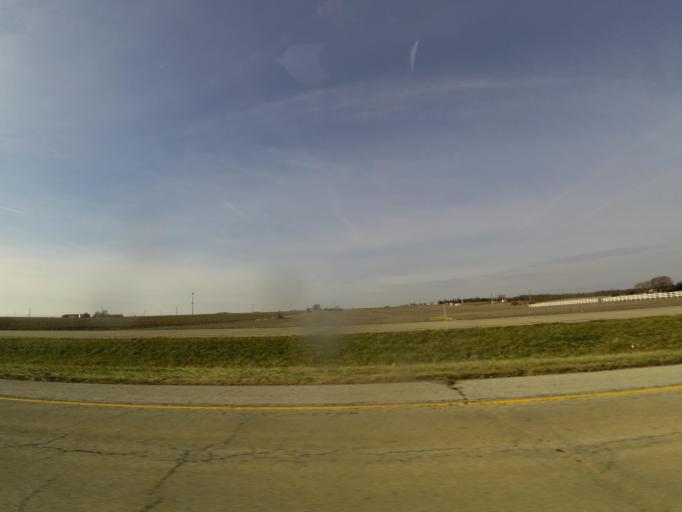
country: US
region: Illinois
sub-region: Macon County
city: Maroa
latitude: 40.0812
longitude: -88.9656
